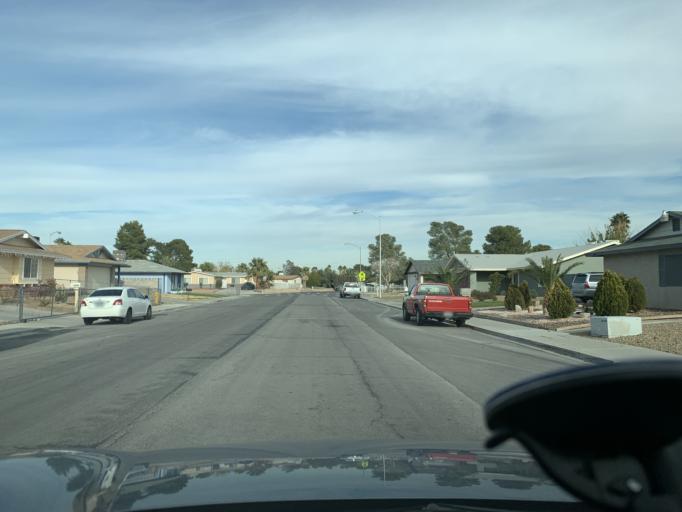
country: US
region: Nevada
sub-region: Clark County
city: Spring Valley
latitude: 36.1096
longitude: -115.2308
